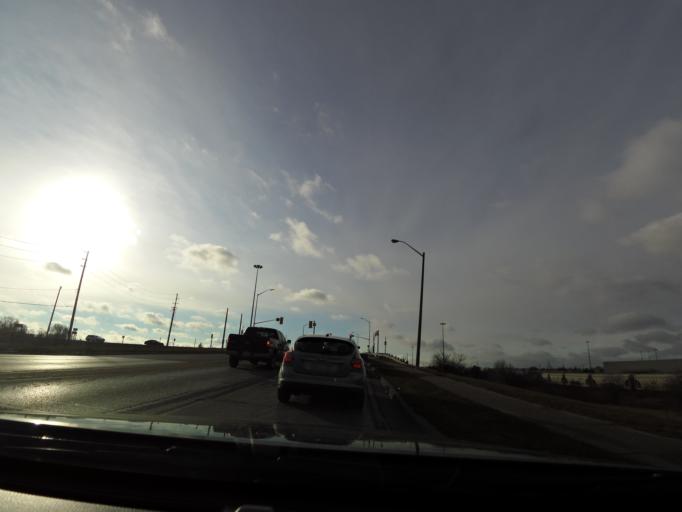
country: CA
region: Ontario
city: Brampton
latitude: 43.7020
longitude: -79.7305
